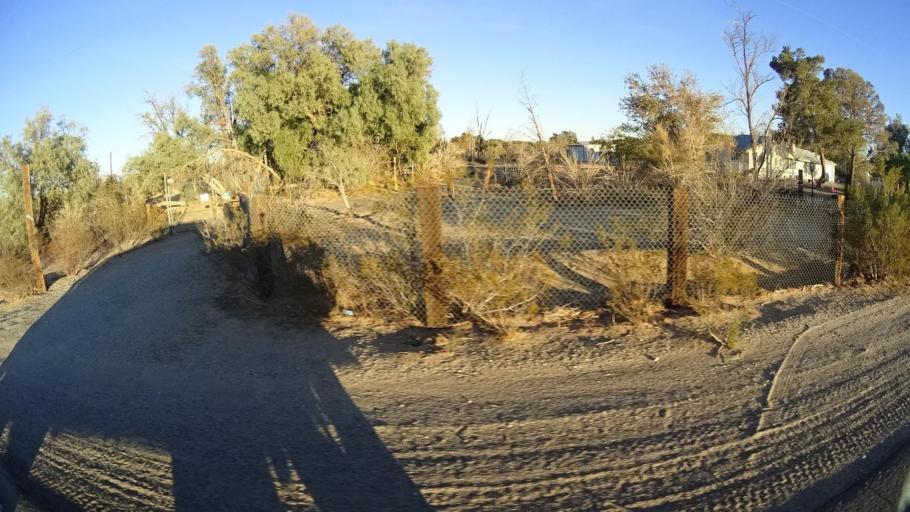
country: US
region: California
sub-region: Kern County
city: Ridgecrest
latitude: 35.6322
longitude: -117.7055
